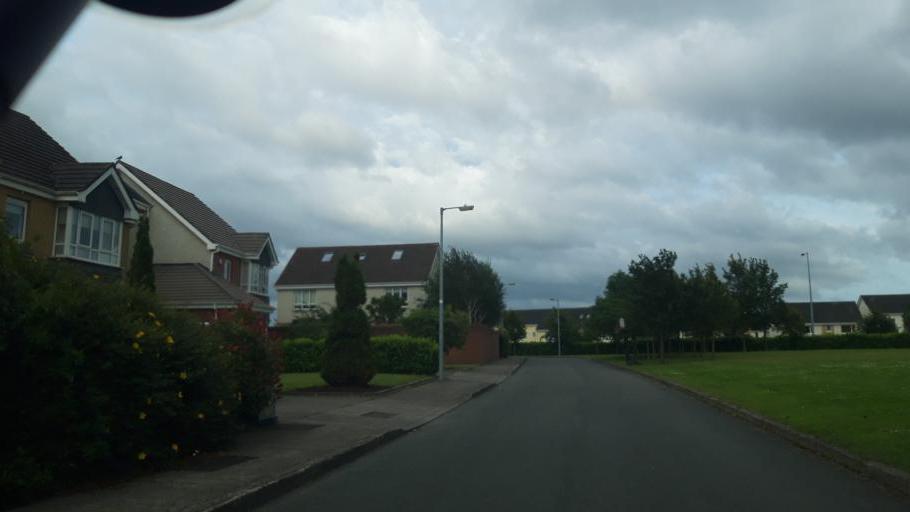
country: IE
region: Leinster
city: Hartstown
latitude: 53.3957
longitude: -6.4451
